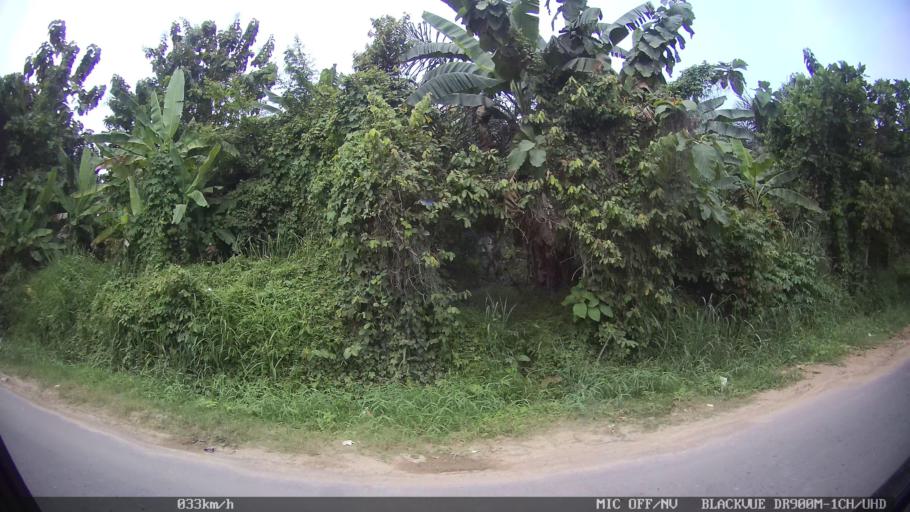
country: ID
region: Lampung
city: Bandarlampung
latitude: -5.4225
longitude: 105.2807
